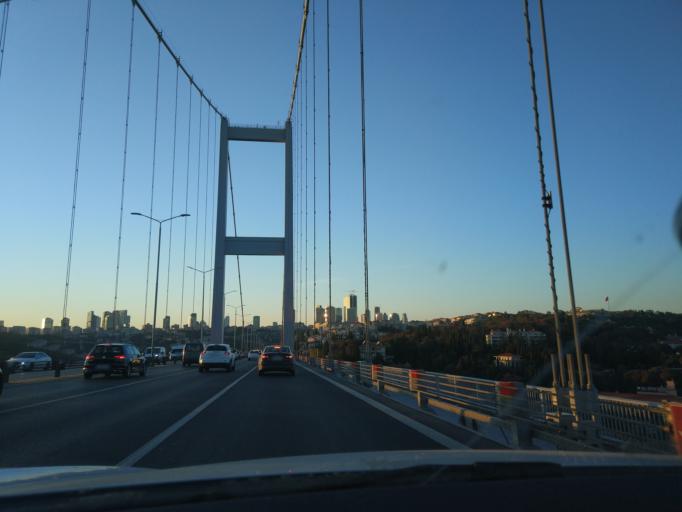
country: TR
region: Istanbul
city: UEskuedar
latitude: 41.0479
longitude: 29.0320
